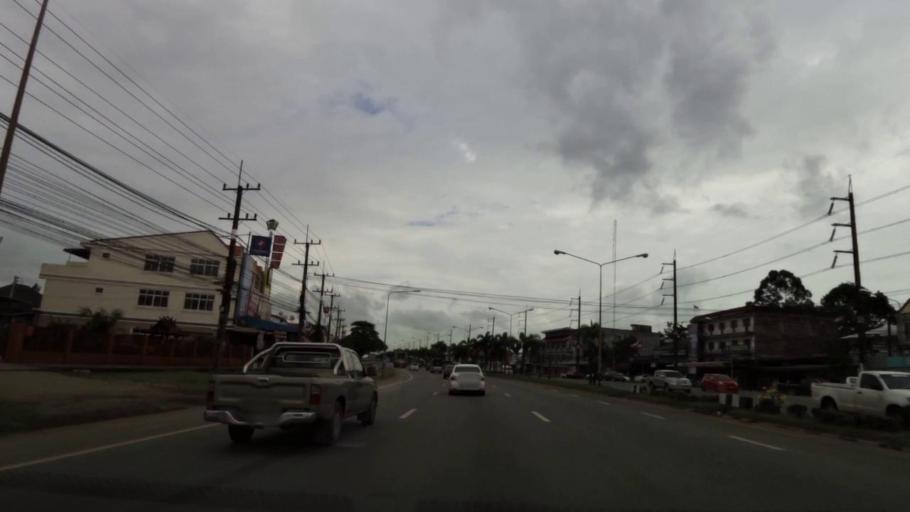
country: TH
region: Chanthaburi
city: Tha Mai
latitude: 12.7215
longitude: 101.9711
